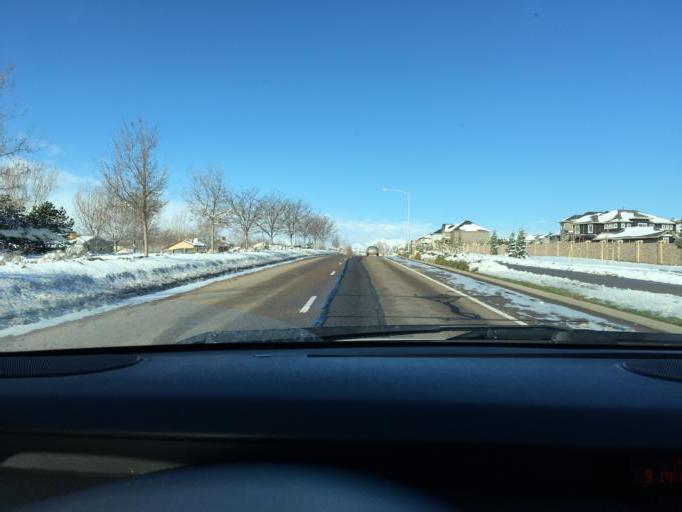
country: US
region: Colorado
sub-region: Adams County
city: Northglenn
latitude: 39.9432
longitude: -105.0021
